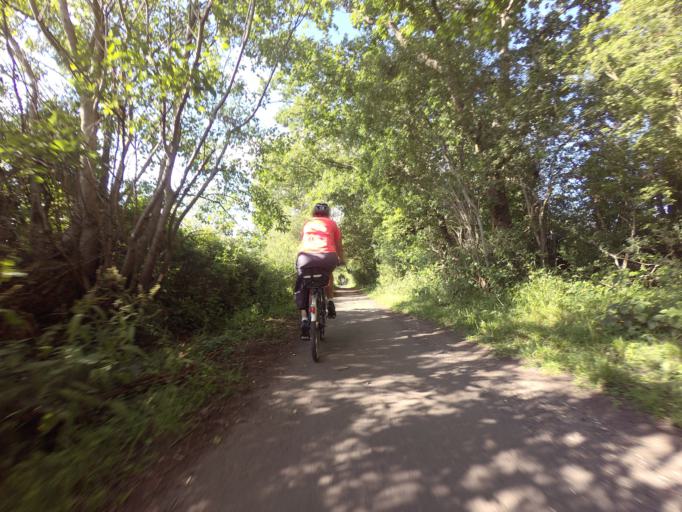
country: GB
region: England
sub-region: East Sussex
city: Hailsham
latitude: 50.8985
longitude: 0.2582
